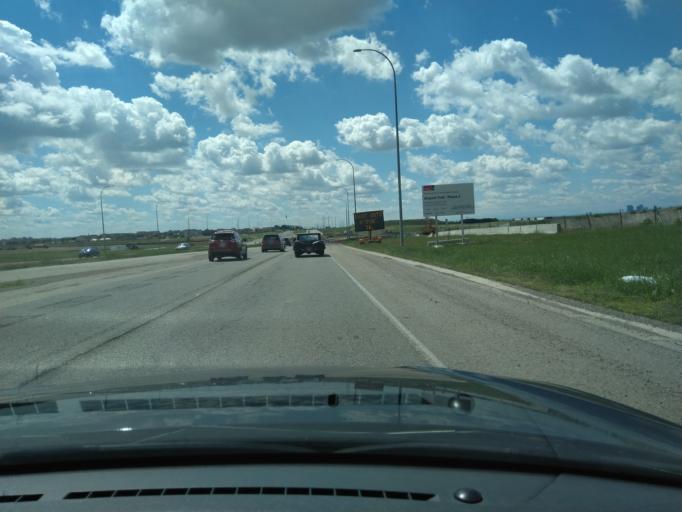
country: CA
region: Alberta
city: Calgary
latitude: 51.1431
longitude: -113.9702
